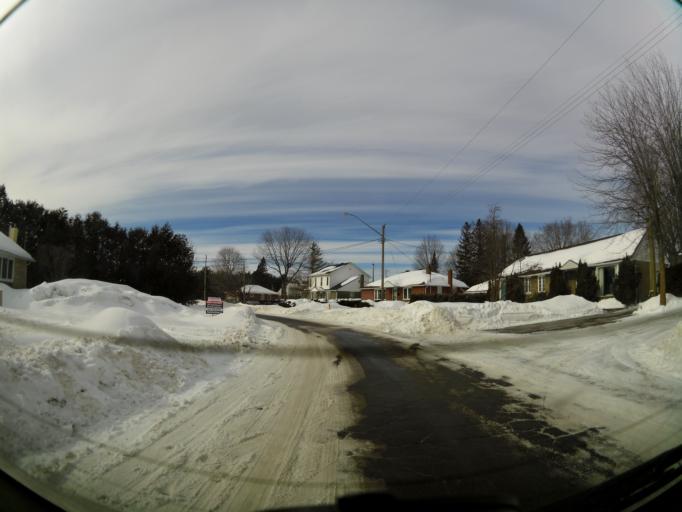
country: CA
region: Ontario
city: Ottawa
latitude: 45.4415
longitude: -75.6110
